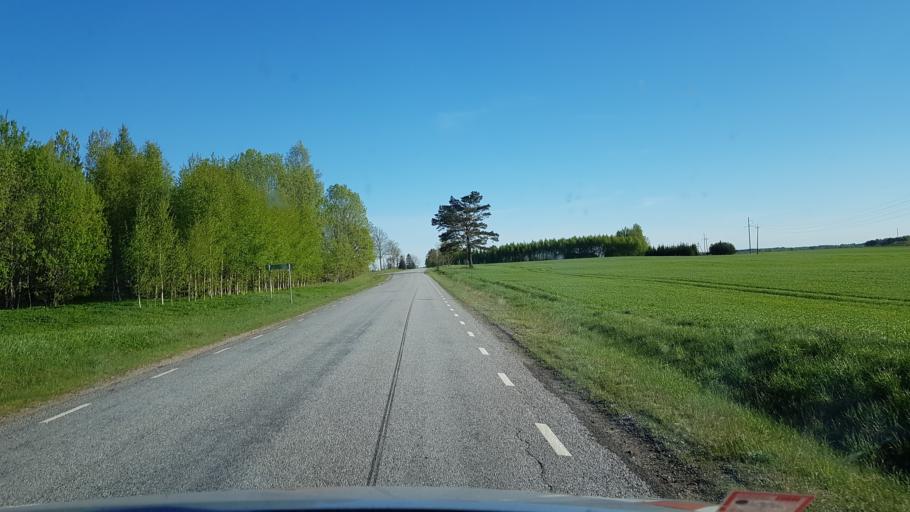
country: EE
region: Vorumaa
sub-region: Voru linn
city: Voru
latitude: 57.9315
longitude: 26.9518
